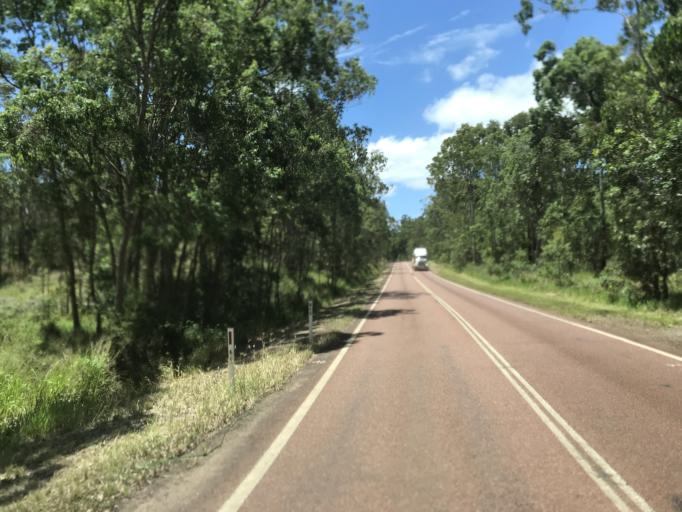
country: AU
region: Queensland
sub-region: Tablelands
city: Ravenshoe
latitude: -17.5926
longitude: 145.4761
